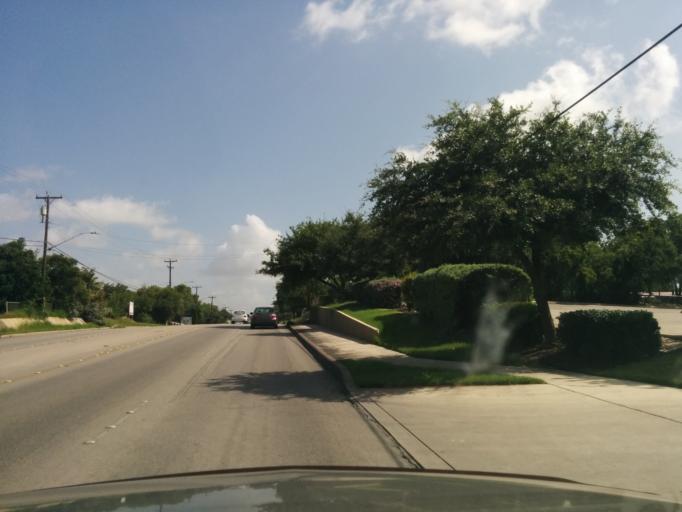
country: US
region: Texas
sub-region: Bexar County
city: Leon Valley
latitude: 29.5470
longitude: -98.6149
